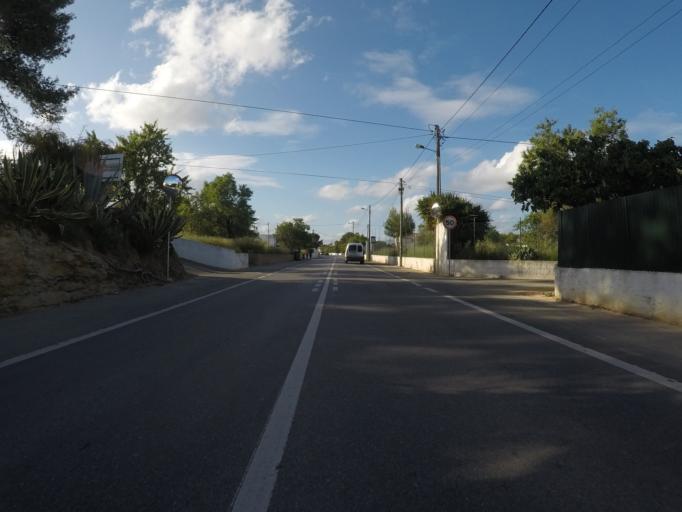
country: PT
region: Faro
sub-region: Lagoa
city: Lagoa
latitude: 37.1137
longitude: -8.4550
